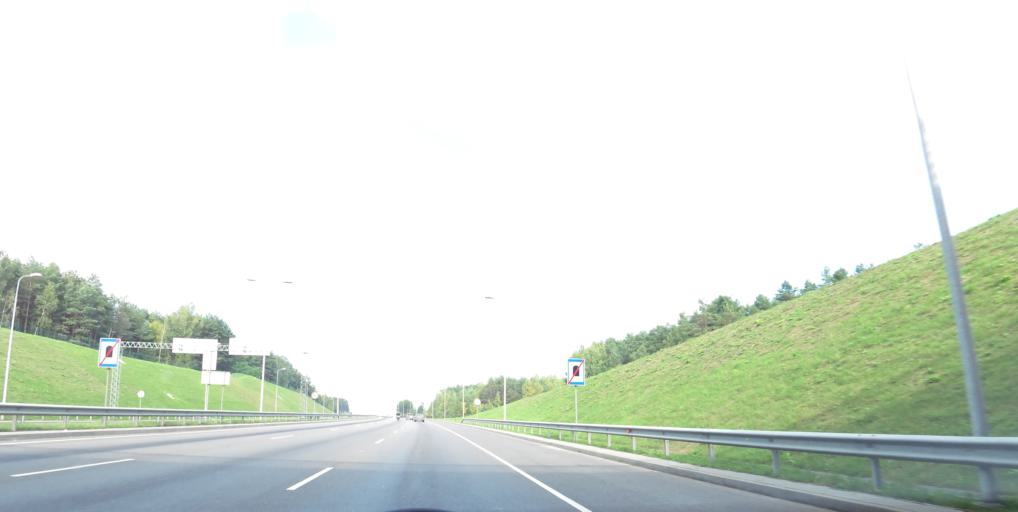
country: LT
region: Vilnius County
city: Lazdynai
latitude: 54.6752
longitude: 25.1962
